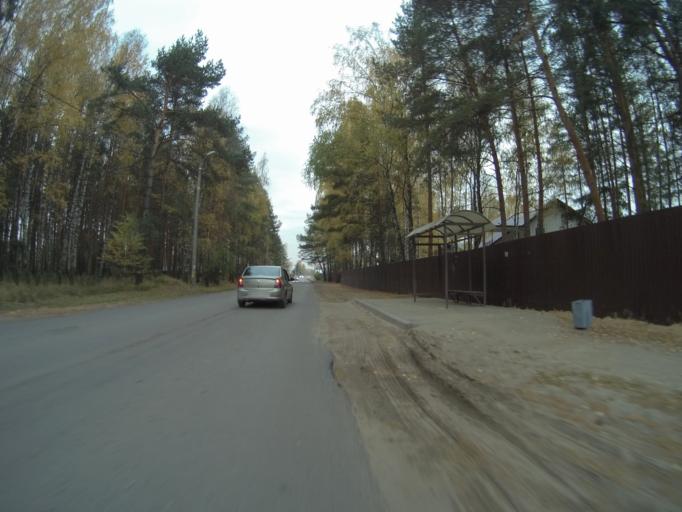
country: RU
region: Vladimir
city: Kommunar
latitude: 56.1139
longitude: 40.4495
